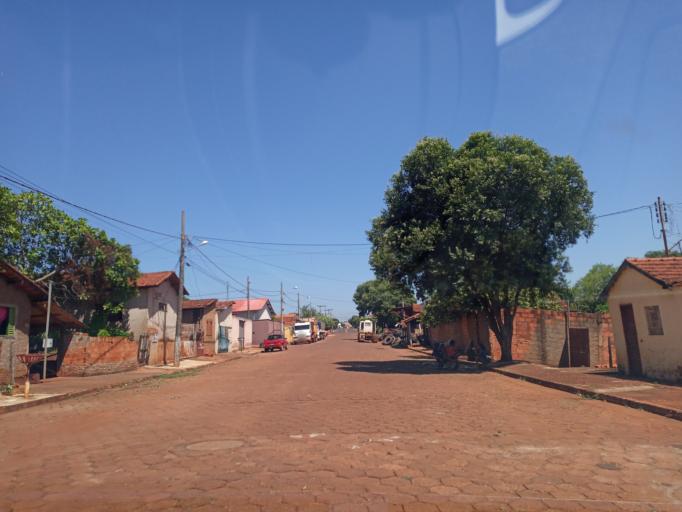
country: BR
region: Minas Gerais
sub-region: Capinopolis
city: Capinopolis
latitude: -18.6783
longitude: -49.5717
